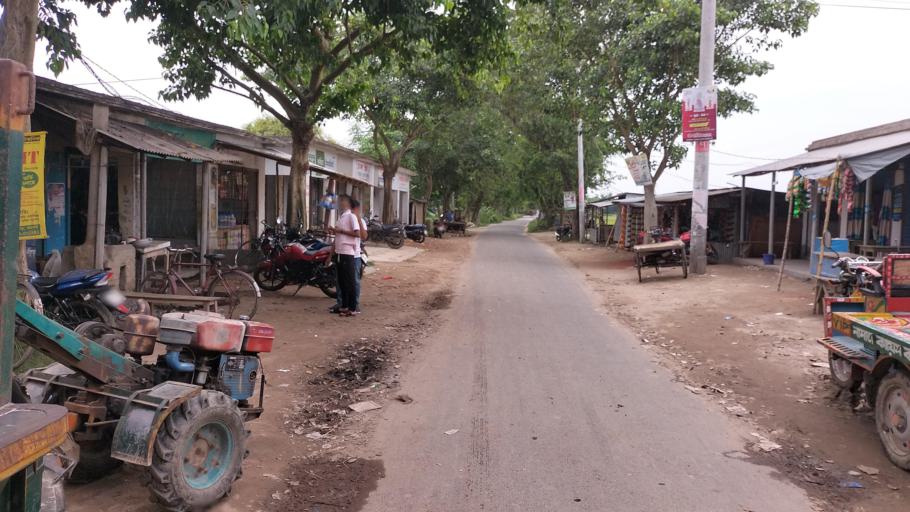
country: BD
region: Rajshahi
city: Rajshahi
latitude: 24.5132
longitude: 88.6359
